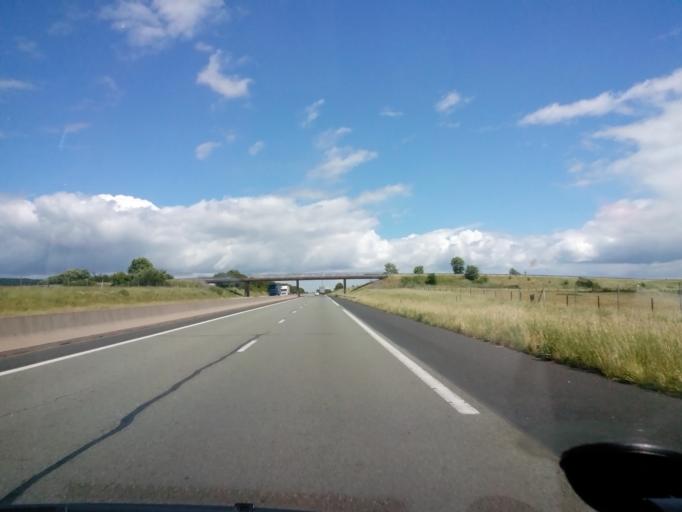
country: FR
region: Lorraine
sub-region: Departement des Vosges
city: Lamarche
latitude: 48.1691
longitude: 5.7165
